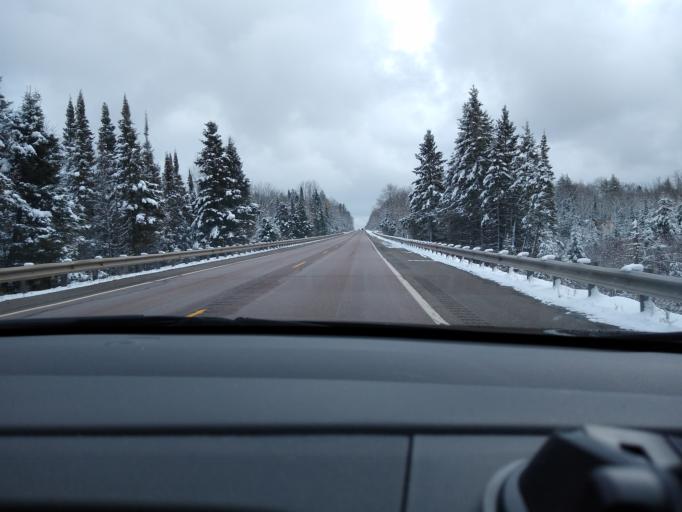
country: US
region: Wisconsin
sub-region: Vilas County
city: Eagle River
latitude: 46.2086
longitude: -89.0304
